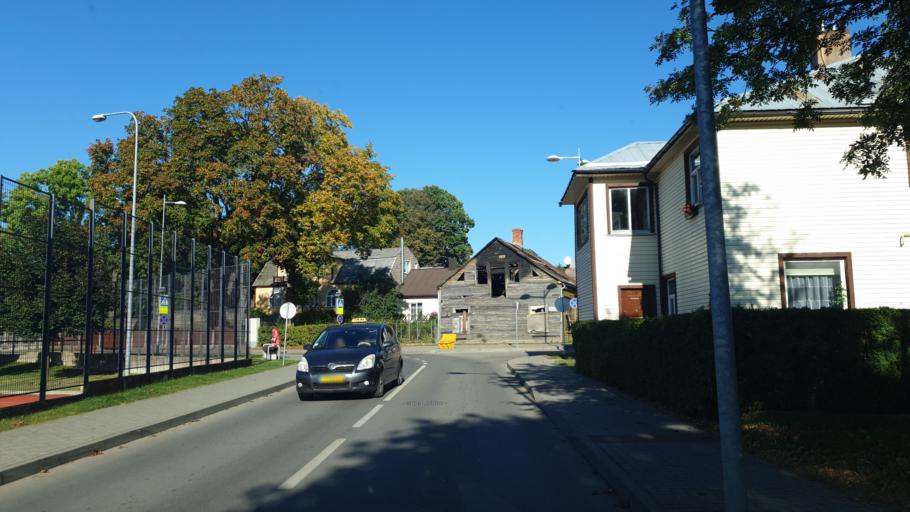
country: LT
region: Telsiu apskritis
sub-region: Telsiai
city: Telsiai
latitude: 55.9851
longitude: 22.2445
